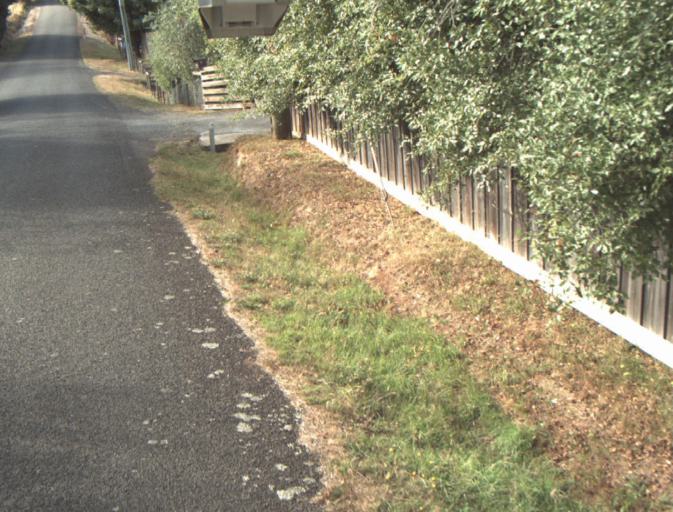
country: AU
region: Tasmania
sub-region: Launceston
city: Mayfield
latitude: -41.2794
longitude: 147.1924
